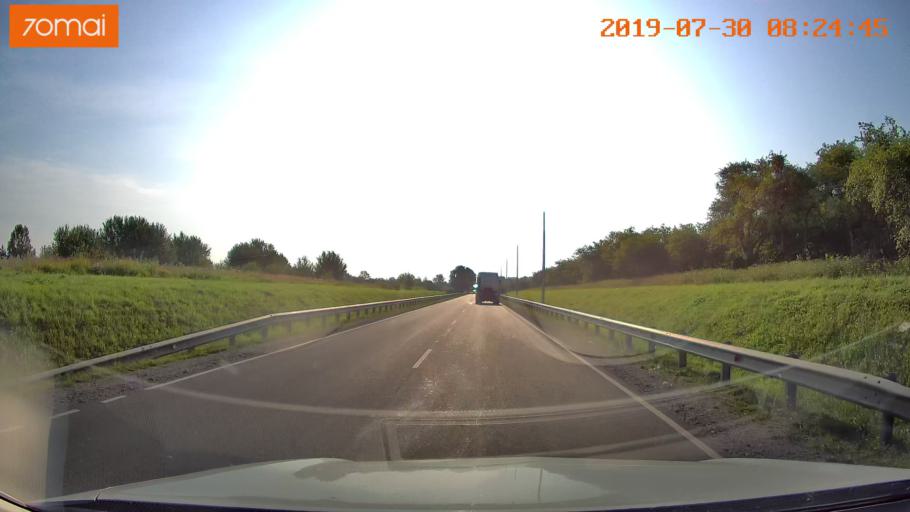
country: RU
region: Kaliningrad
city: Chernyakhovsk
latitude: 54.6237
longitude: 21.5652
